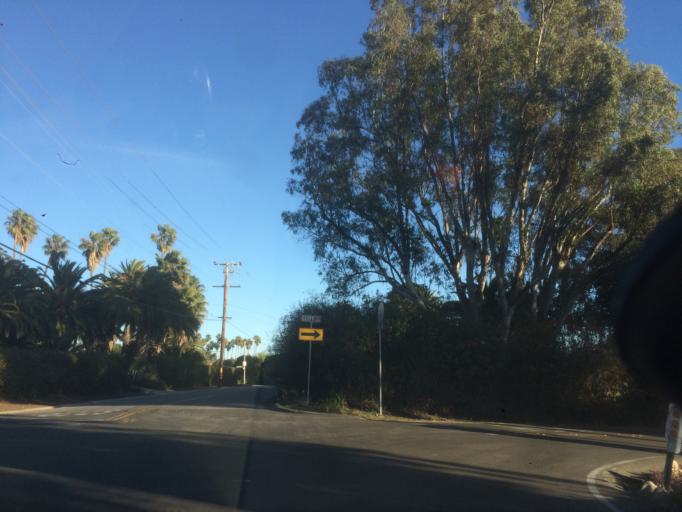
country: US
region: California
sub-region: Santa Barbara County
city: Santa Barbara
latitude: 34.4089
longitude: -119.7564
